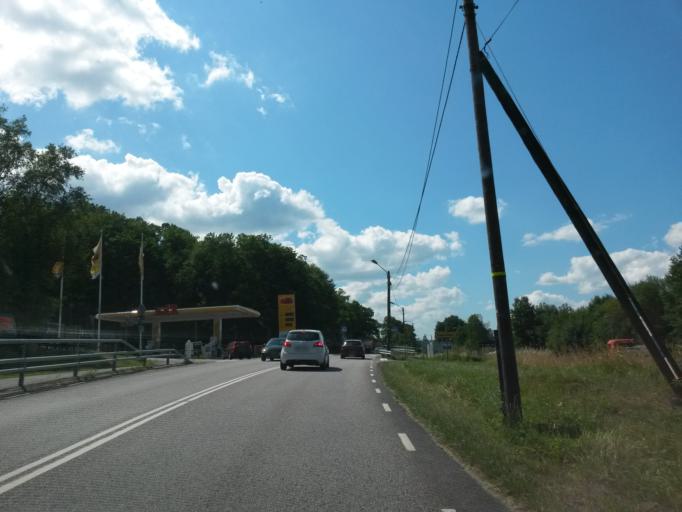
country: SE
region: Vaestra Goetaland
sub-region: Partille Kommun
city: Partille
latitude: 57.7985
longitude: 12.1465
